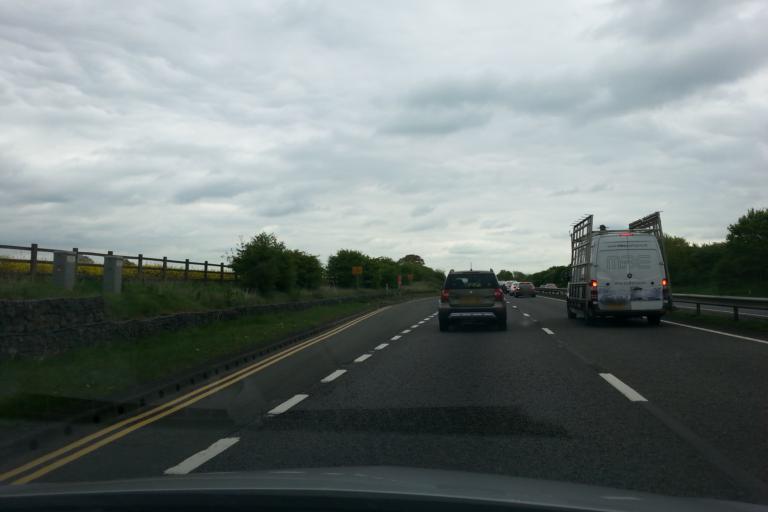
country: GB
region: England
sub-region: Leicestershire
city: Castle Donington
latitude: 52.7983
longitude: -1.3657
